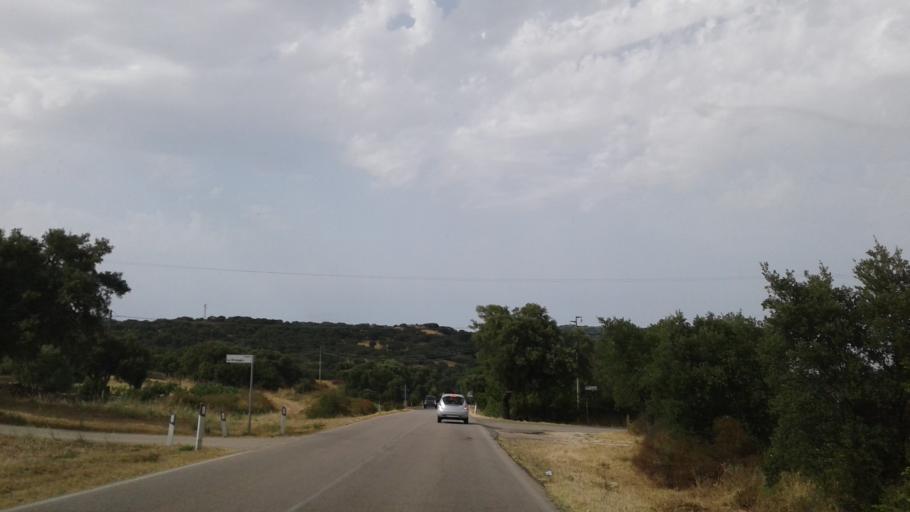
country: IT
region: Sardinia
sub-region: Provincia di Olbia-Tempio
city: Sant'Antonio di Gallura
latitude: 40.9564
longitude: 9.2945
